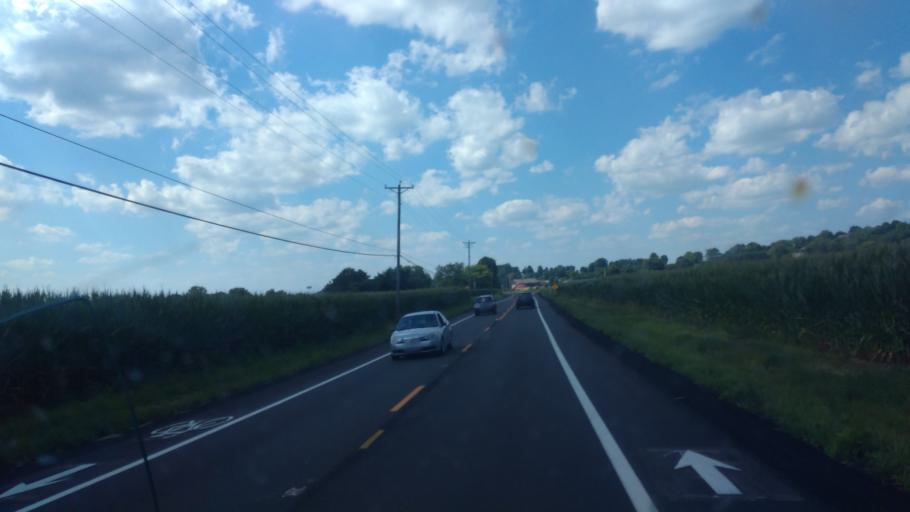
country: US
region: Ohio
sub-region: Tuscarawas County
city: Strasburg
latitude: 40.6341
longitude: -81.4384
